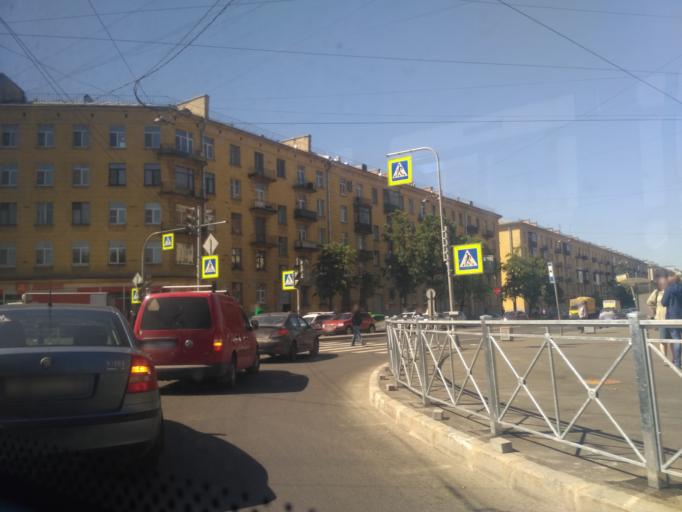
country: RU
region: Leningrad
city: Kalininskiy
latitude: 59.9598
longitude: 30.4222
